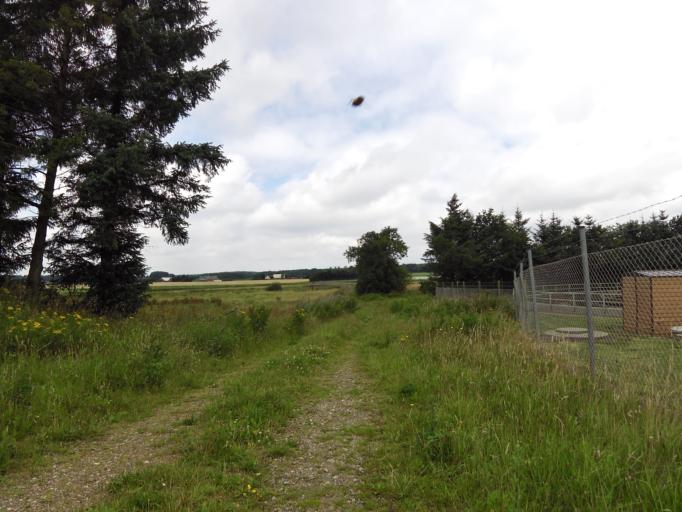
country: DK
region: South Denmark
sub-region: Haderslev Kommune
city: Gram
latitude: 55.2964
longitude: 9.0412
